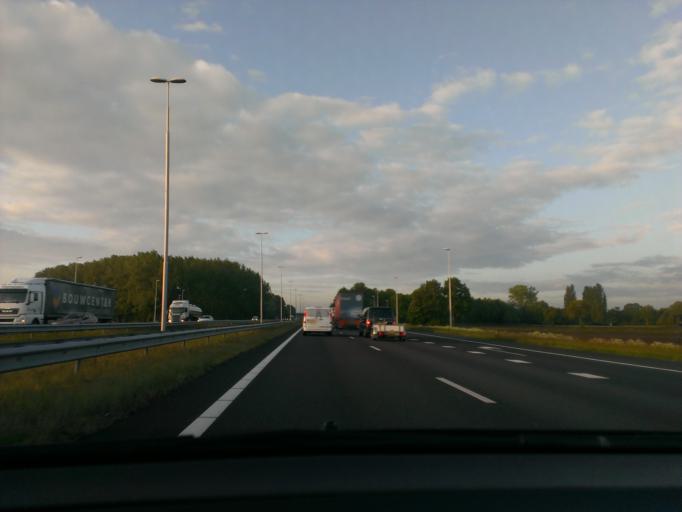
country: NL
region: Gelderland
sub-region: Gemeente Epe
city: Emst
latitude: 52.2965
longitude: 6.0091
